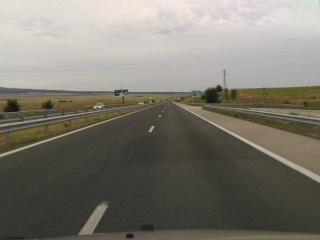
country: BG
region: Stara Zagora
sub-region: Obshtina Chirpan
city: Chirpan
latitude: 42.2348
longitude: 25.3642
